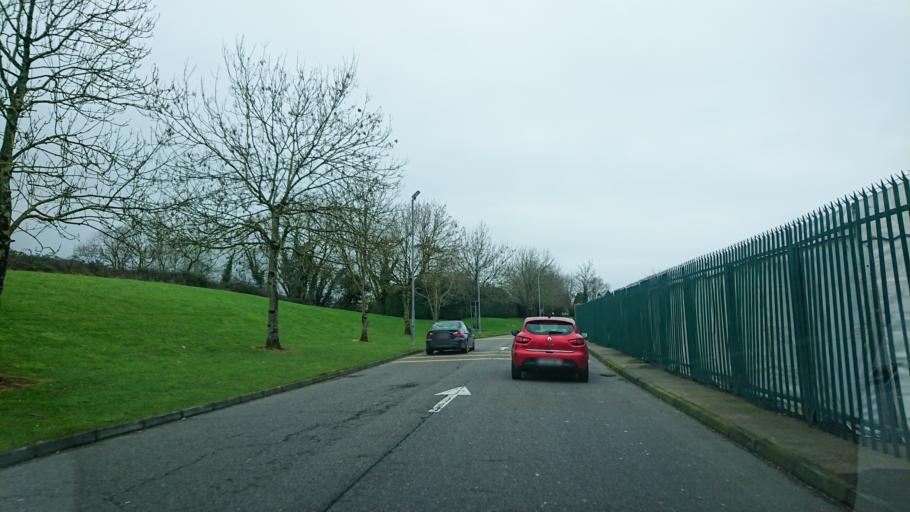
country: IE
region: Munster
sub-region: County Cork
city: Cork
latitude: 51.8731
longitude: -8.5202
